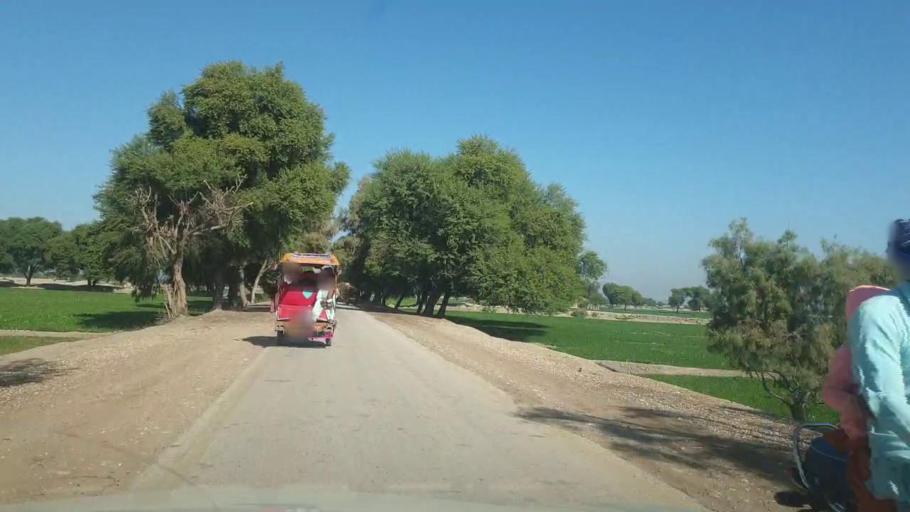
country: PK
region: Sindh
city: Bhan
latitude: 26.5513
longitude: 67.6336
